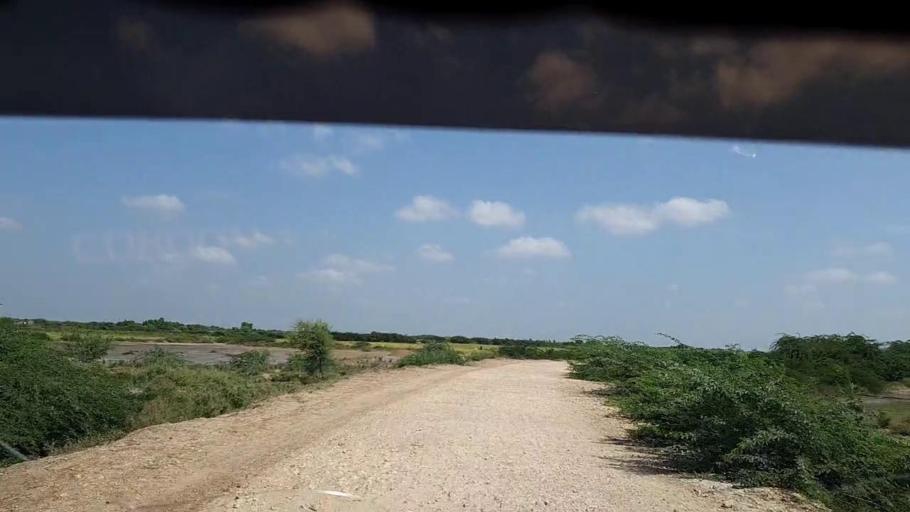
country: PK
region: Sindh
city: Kadhan
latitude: 24.6035
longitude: 68.9844
